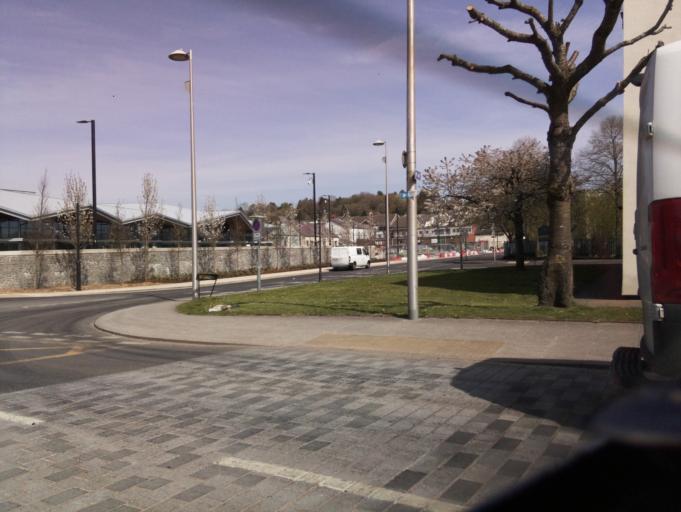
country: GB
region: Wales
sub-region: Merthyr Tydfil County Borough
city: Merthyr Tydfil
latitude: 51.7437
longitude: -3.3807
